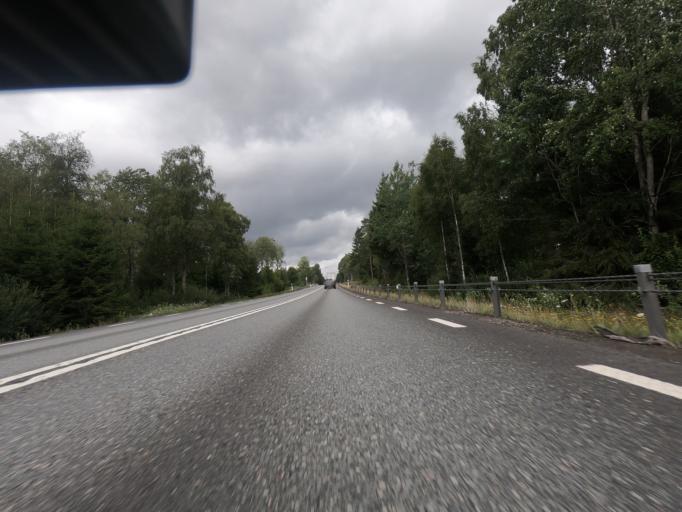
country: SE
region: Joenkoeping
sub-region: Savsjo Kommun
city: Vrigstad
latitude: 57.3990
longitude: 14.3735
